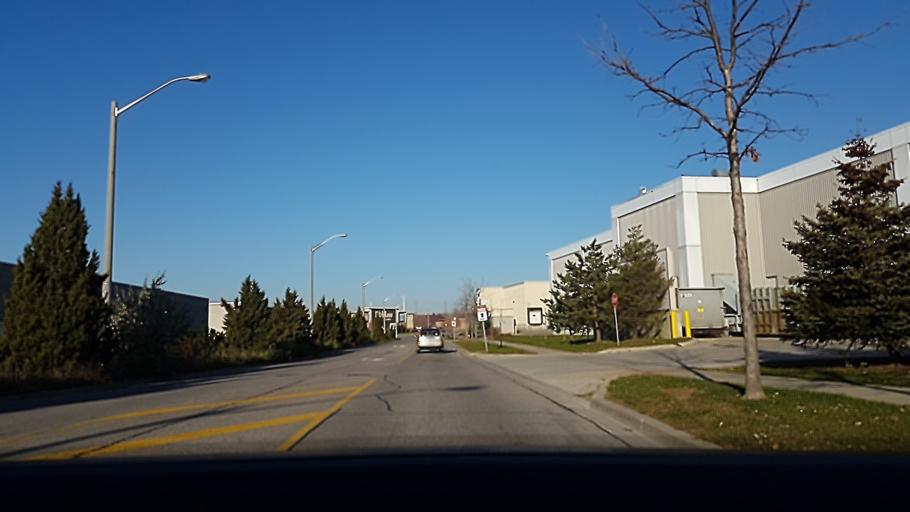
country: CA
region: Ontario
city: Concord
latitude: 43.7842
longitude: -79.4720
